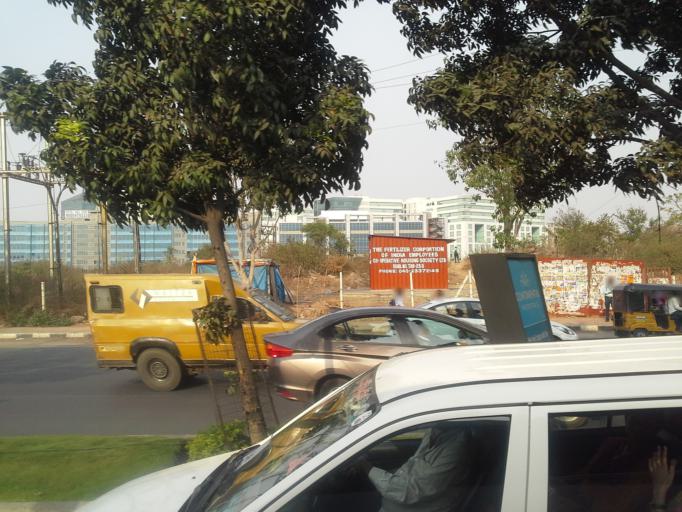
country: IN
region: Telangana
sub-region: Medak
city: Serilingampalle
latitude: 17.4445
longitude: 78.3533
